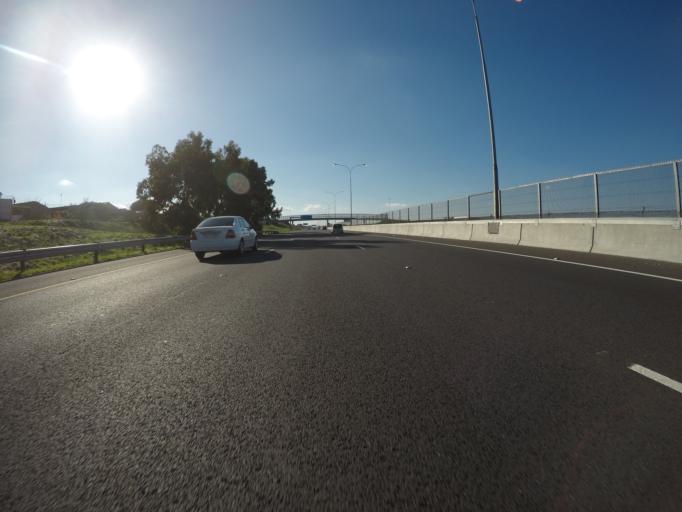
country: ZA
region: Western Cape
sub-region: City of Cape Town
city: Kraaifontein
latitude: -33.9697
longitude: 18.6542
